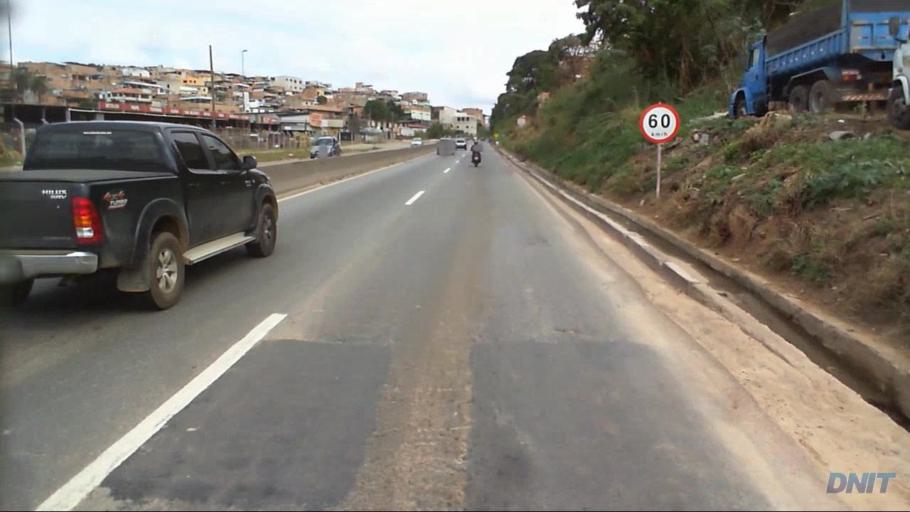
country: BR
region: Minas Gerais
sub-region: Santa Luzia
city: Santa Luzia
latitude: -19.8481
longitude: -43.8879
